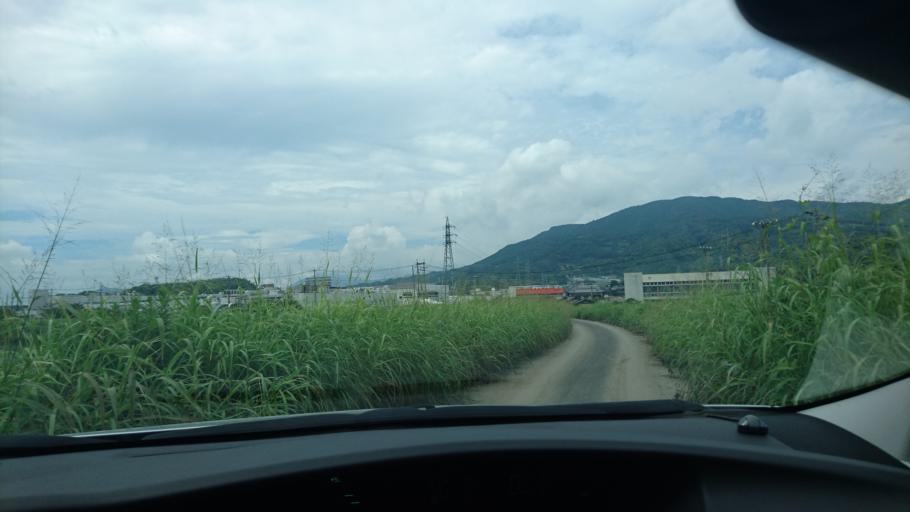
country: JP
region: Saga Prefecture
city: Takeocho-takeo
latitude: 33.2102
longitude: 130.1116
